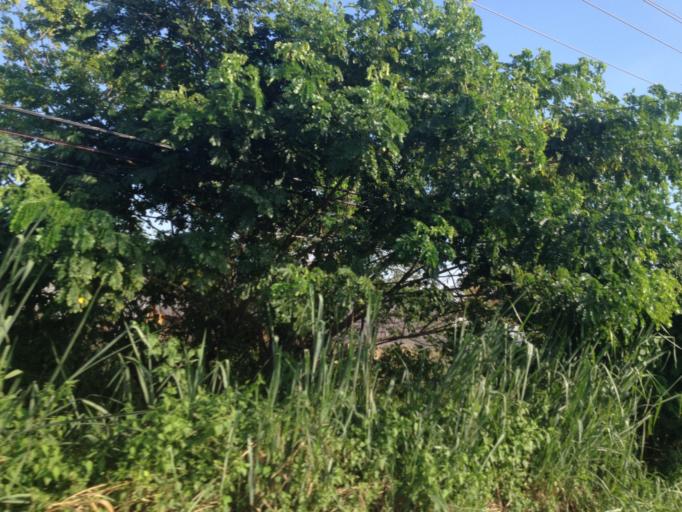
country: TH
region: Chiang Mai
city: Hang Dong
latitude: 18.7327
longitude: 98.9266
